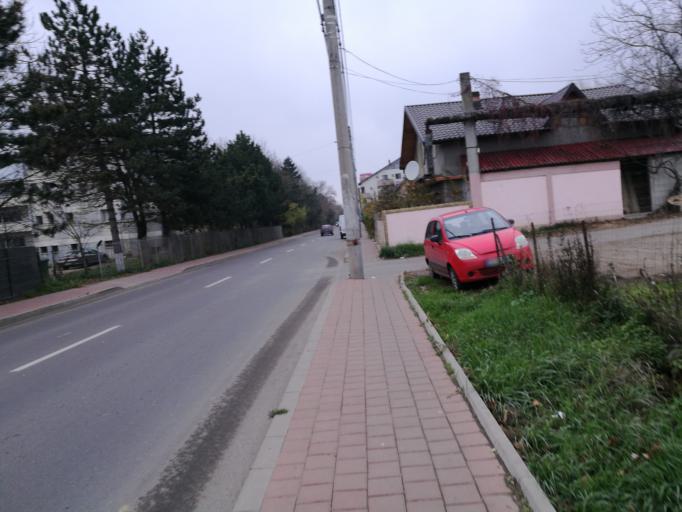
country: RO
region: Suceava
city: Suceava
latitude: 47.6694
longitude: 26.2713
